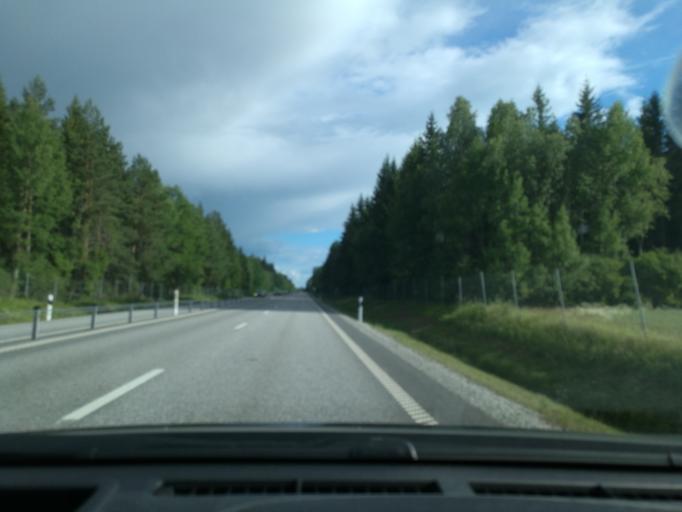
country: SE
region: Vaestmanland
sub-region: Surahammars Kommun
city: Ramnas
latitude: 59.7462
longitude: 16.2260
